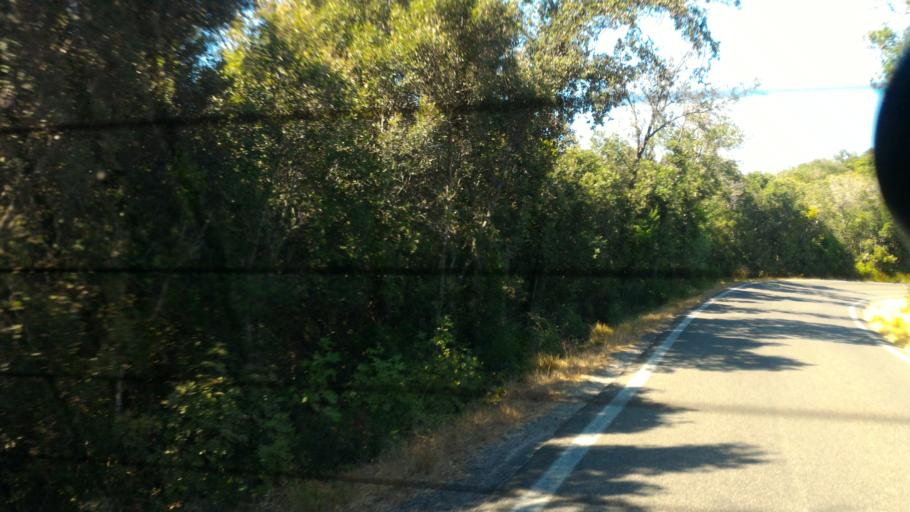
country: IT
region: Tuscany
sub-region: Provincia di Grosseto
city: Porto Ercole
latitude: 42.4241
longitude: 11.1749
